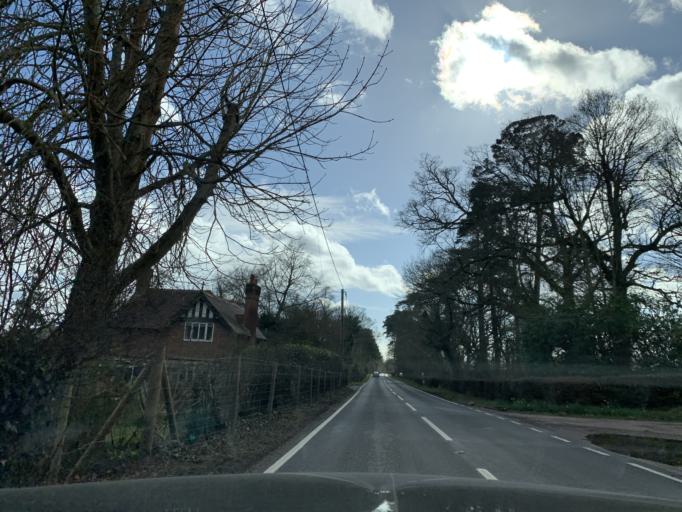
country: GB
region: England
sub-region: West Sussex
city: Crawley Down
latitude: 51.0832
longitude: -0.0776
